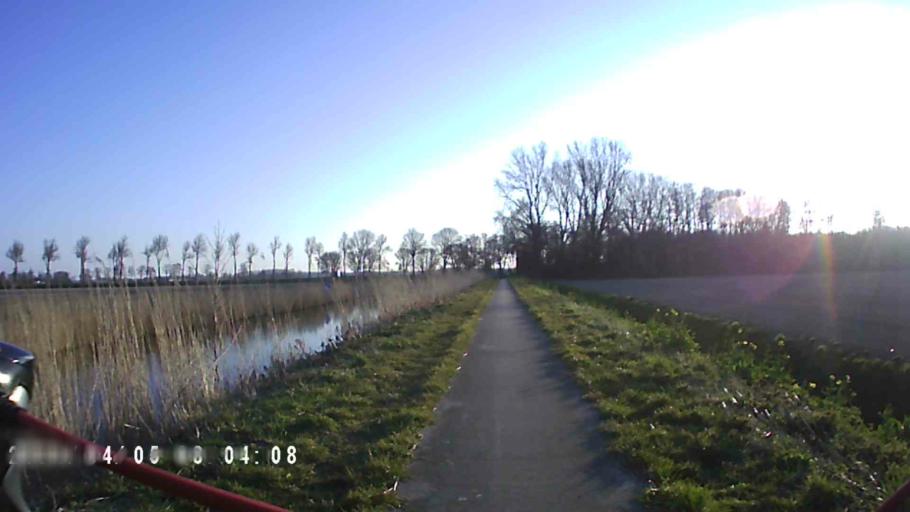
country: NL
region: Groningen
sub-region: Gemeente Zuidhorn
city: Oldehove
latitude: 53.3504
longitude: 6.4401
